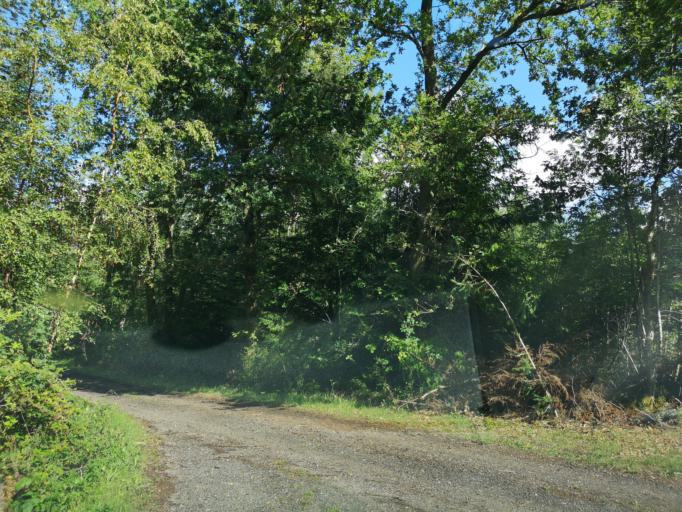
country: DK
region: Central Jutland
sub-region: Holstebro Kommune
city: Holstebro
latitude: 56.3345
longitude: 8.6352
